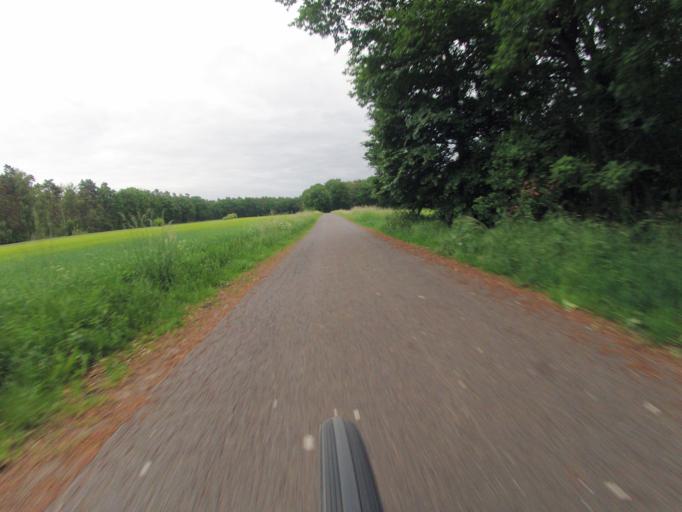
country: DE
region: North Rhine-Westphalia
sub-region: Regierungsbezirk Munster
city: Dreierwalde
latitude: 52.2466
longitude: 7.5340
